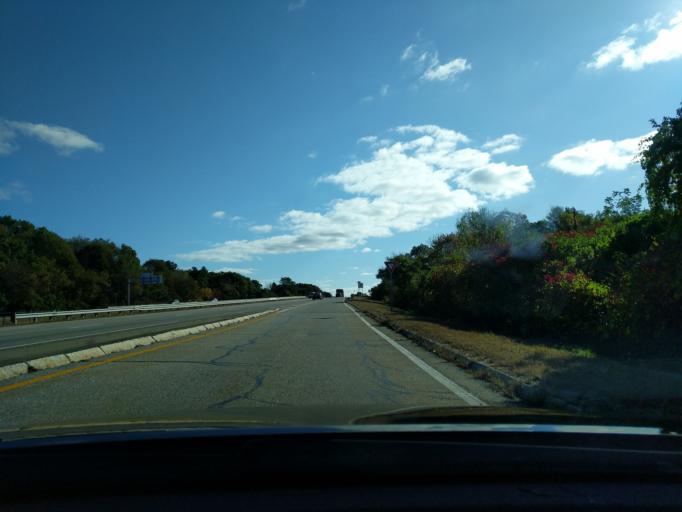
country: US
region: Massachusetts
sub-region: Middlesex County
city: Lexington
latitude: 42.4215
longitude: -71.2339
